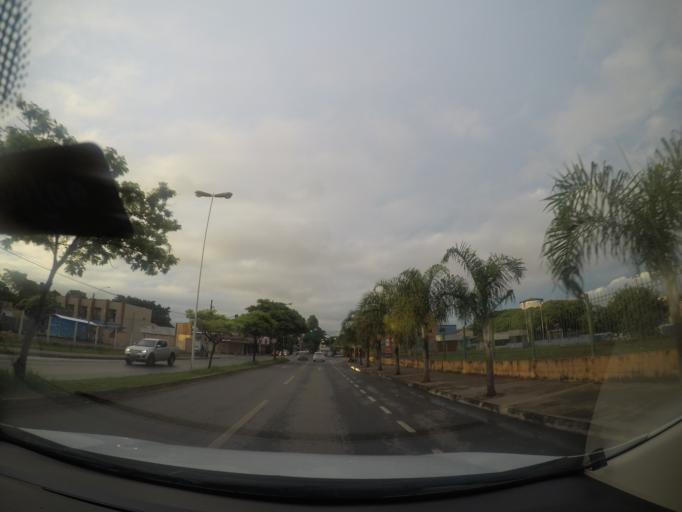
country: BR
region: Goias
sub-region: Goiania
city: Goiania
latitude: -16.6907
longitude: -49.3109
